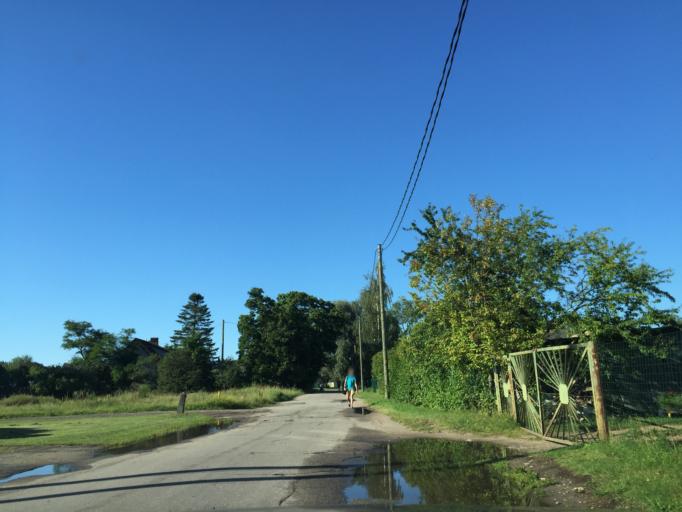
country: LV
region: Riga
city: Jaunciems
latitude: 57.0570
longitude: 24.1383
